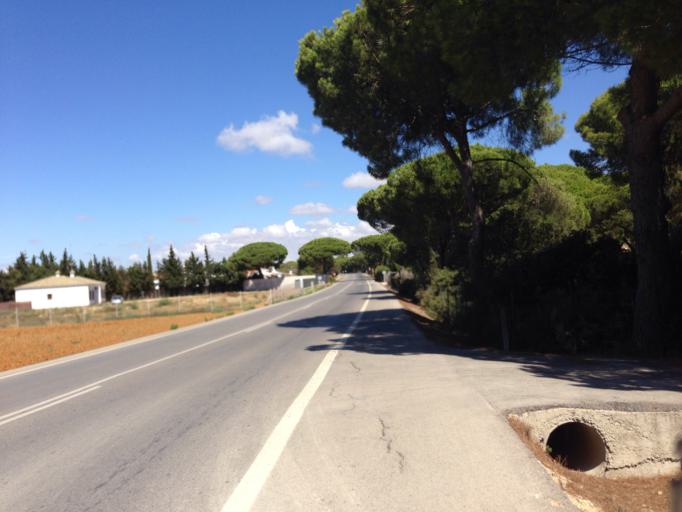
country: ES
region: Andalusia
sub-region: Provincia de Cadiz
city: Conil de la Frontera
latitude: 36.3134
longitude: -6.1053
